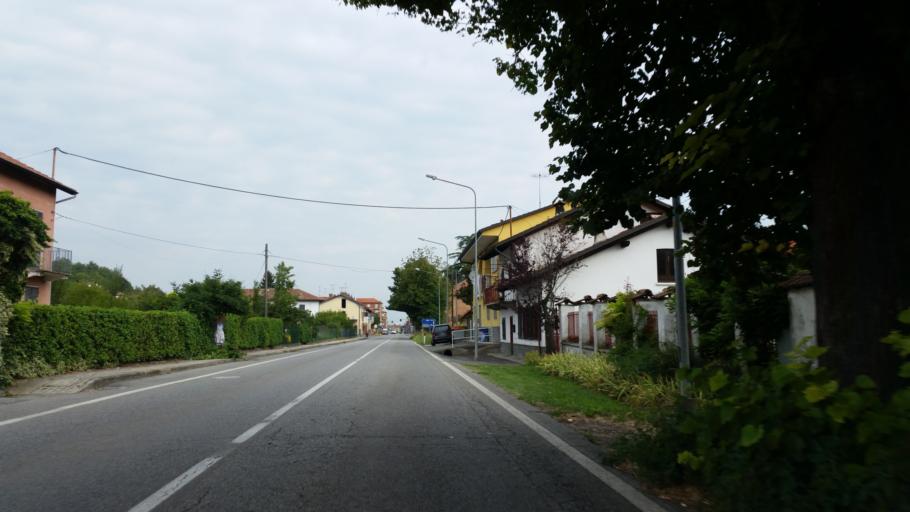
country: IT
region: Piedmont
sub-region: Provincia di Torino
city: Cavagnolo
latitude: 45.1494
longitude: 8.0534
